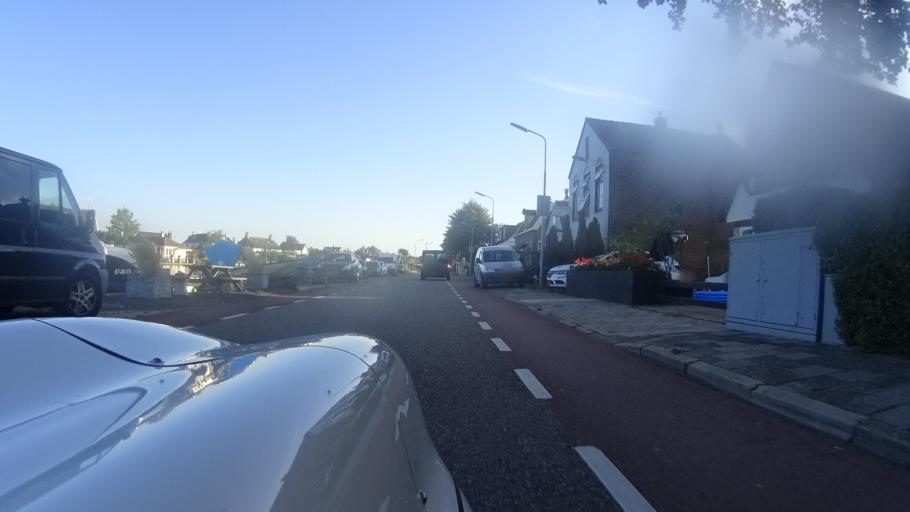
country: NL
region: North Holland
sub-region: Gemeente Aalsmeer
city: Aalsmeer
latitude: 52.2605
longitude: 4.7221
